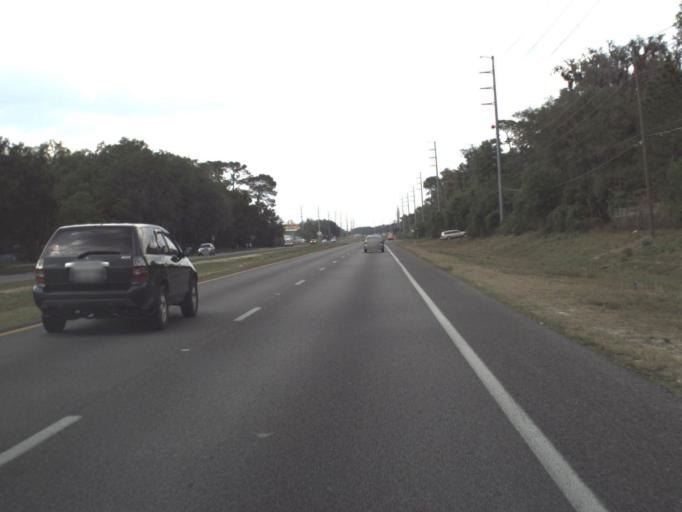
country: US
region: Florida
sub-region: Lake County
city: Eustis
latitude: 28.8774
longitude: -81.6876
